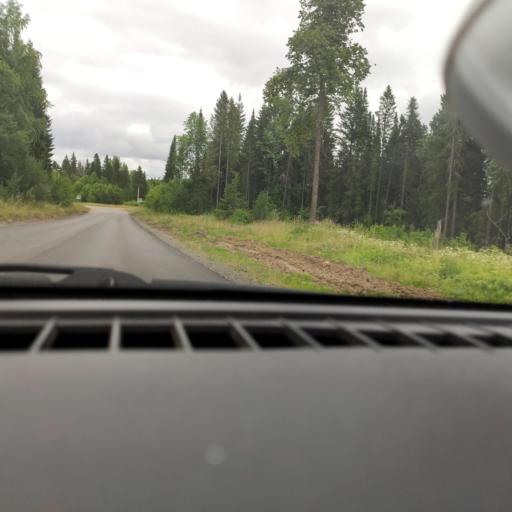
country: RU
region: Perm
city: Polazna
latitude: 58.3410
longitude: 56.2290
